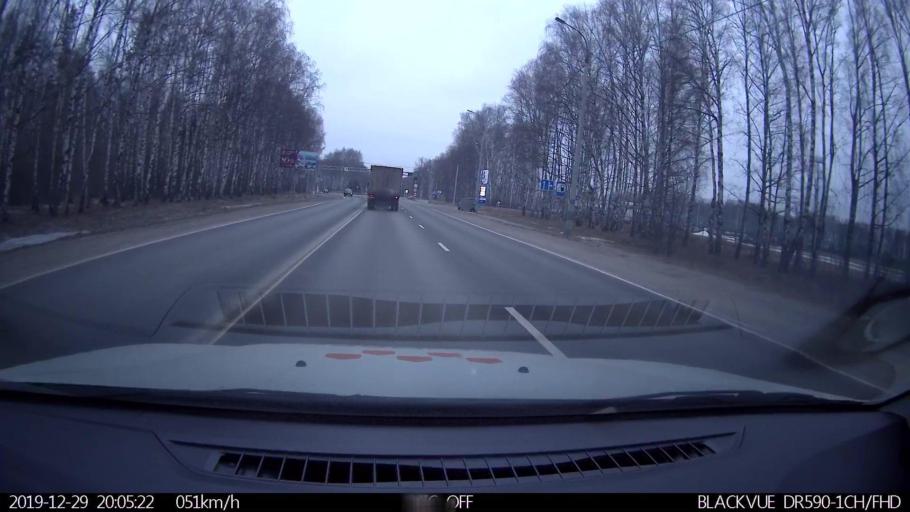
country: RU
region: Nizjnij Novgorod
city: Neklyudovo
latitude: 56.3907
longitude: 44.0107
